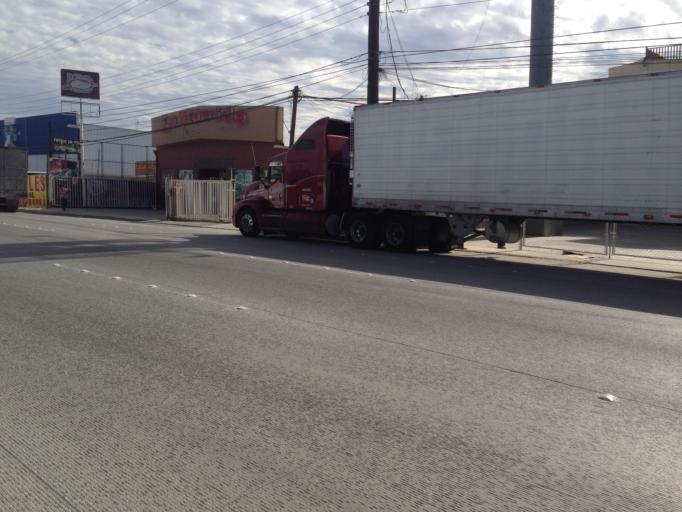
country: MX
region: Baja California
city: Tijuana
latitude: 32.5432
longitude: -116.9447
